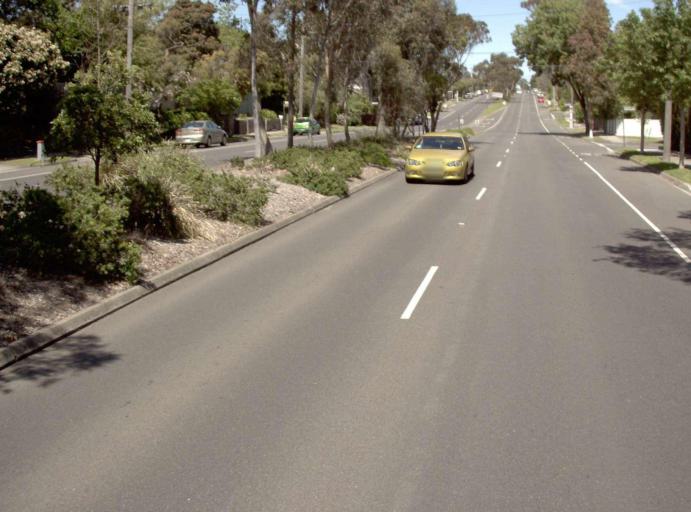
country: AU
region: Victoria
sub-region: Whitehorse
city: Blackburn South
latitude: -37.8339
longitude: 145.1564
